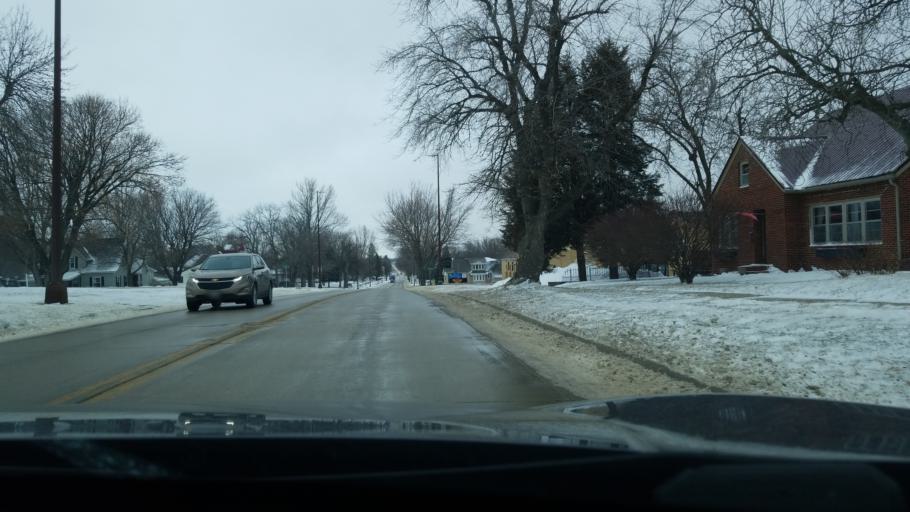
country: US
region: Iowa
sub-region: Lyon County
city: Rock Rapids
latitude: 43.4255
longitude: -96.1757
